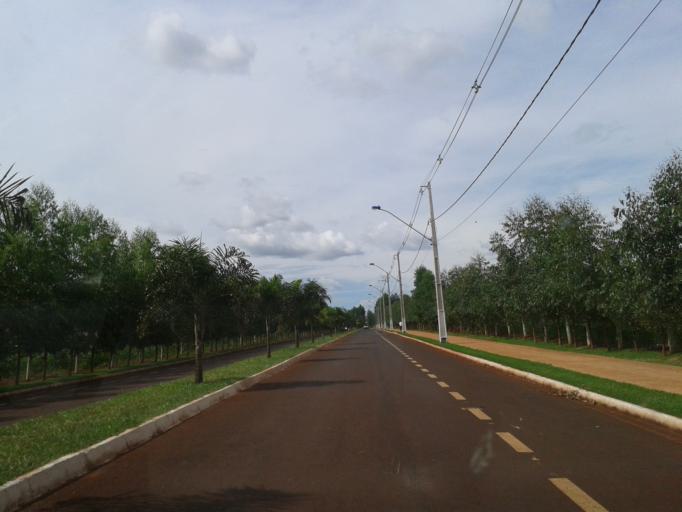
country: BR
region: Minas Gerais
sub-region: Centralina
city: Centralina
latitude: -18.5769
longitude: -49.1977
